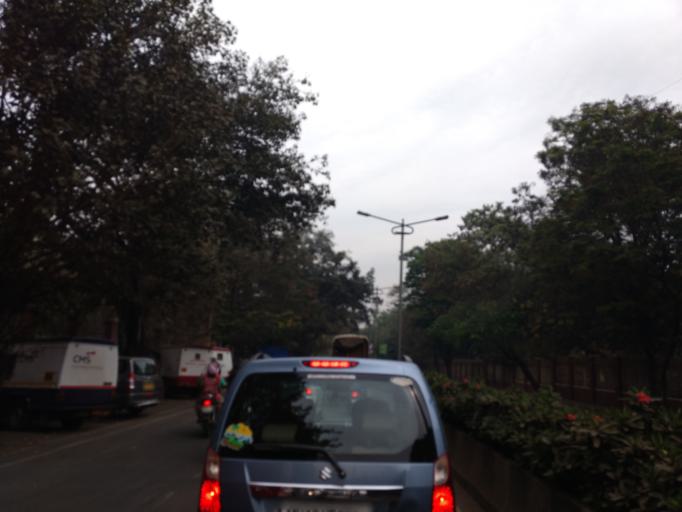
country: IN
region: Maharashtra
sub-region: Pune Division
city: Pune
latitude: 18.5253
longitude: 73.8788
